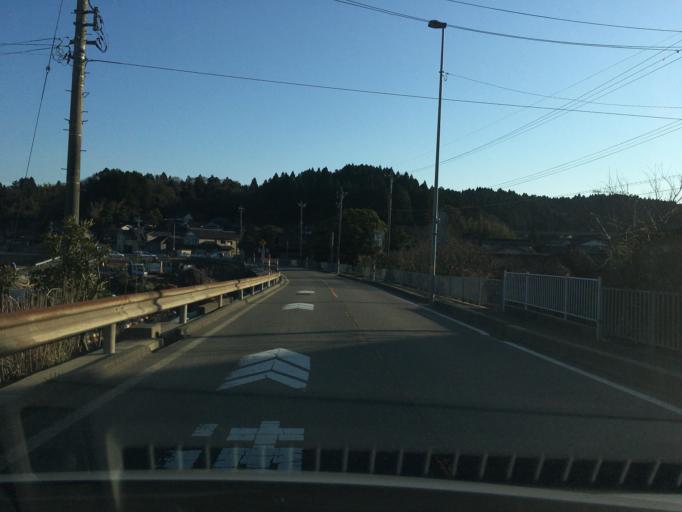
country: JP
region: Ishikawa
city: Nanao
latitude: 36.9785
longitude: 137.0500
